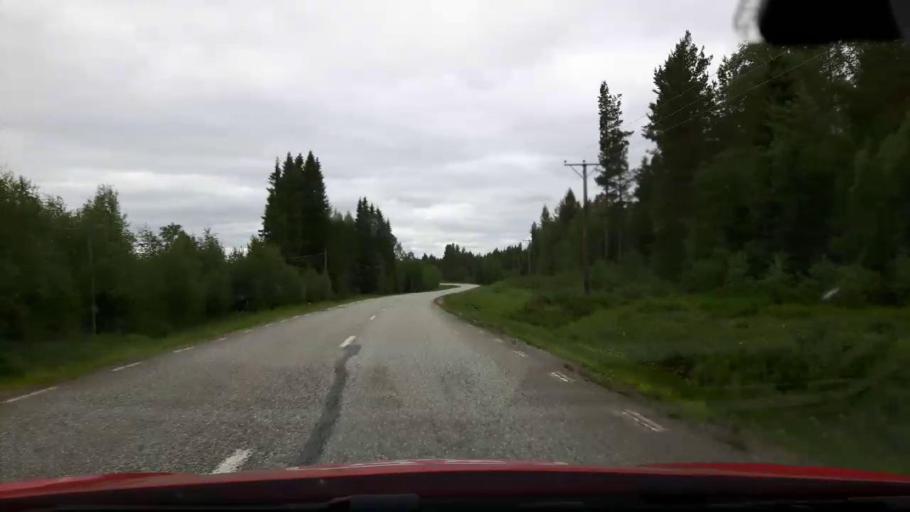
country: SE
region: Jaemtland
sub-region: Stroemsunds Kommun
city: Stroemsund
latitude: 63.3129
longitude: 15.7619
